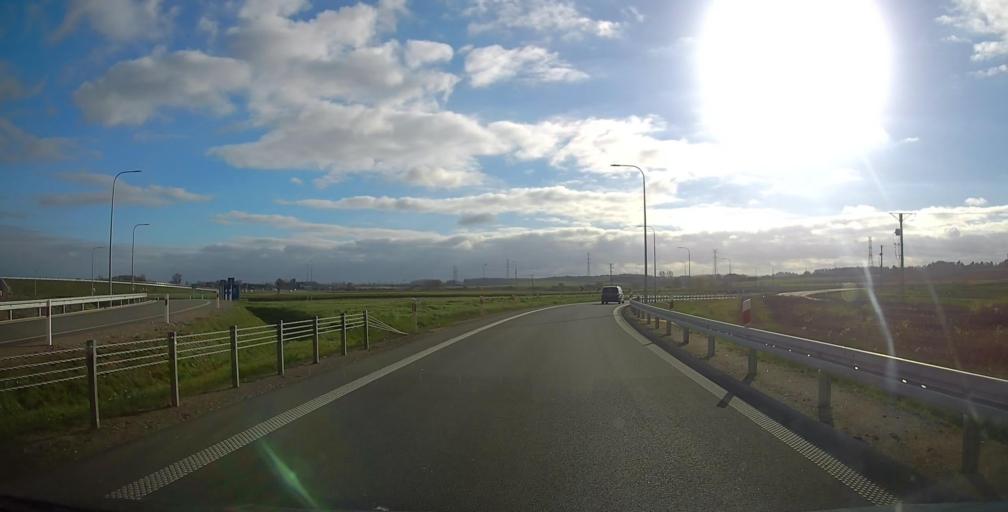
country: PL
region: Warmian-Masurian Voivodeship
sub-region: Powiat elcki
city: Elk
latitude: 53.7564
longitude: 22.3362
